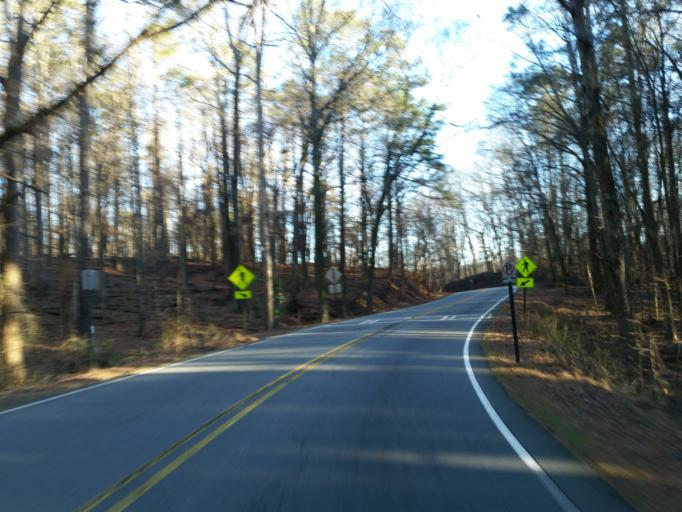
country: US
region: Georgia
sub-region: Cobb County
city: Marietta
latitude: 33.9624
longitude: -84.5885
